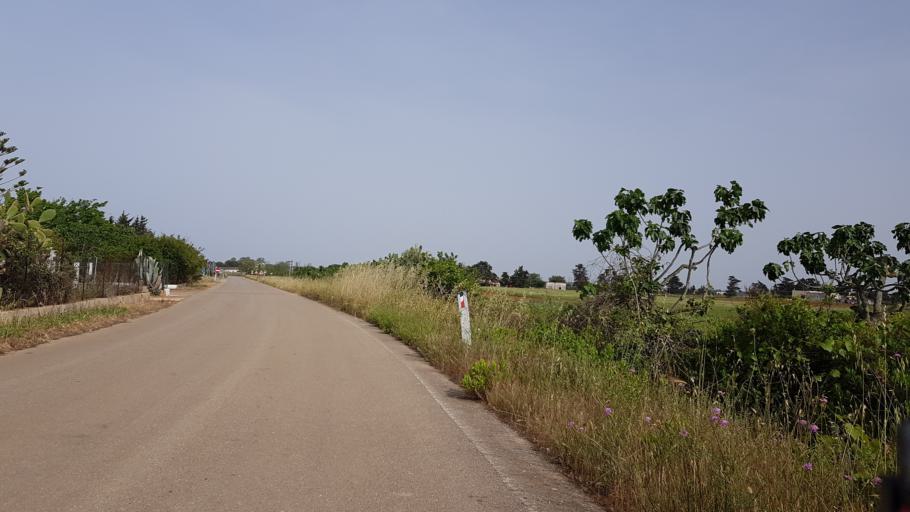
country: IT
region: Apulia
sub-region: Provincia di Brindisi
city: Brindisi
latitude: 40.6689
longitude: 17.8587
